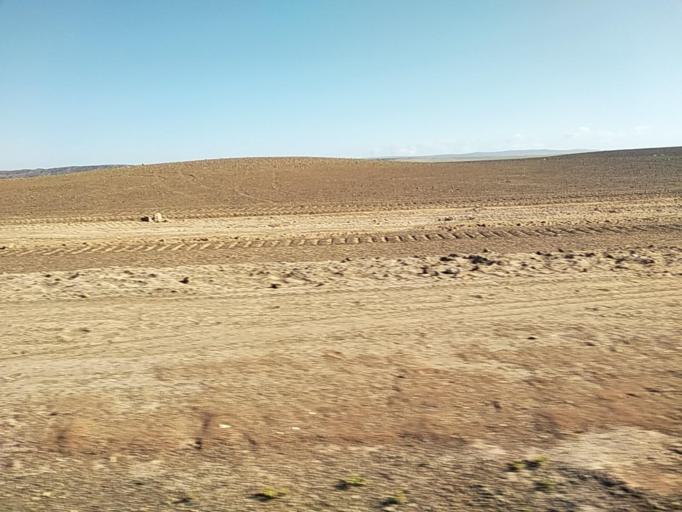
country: CL
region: Atacama
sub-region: Provincia de Copiapo
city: Copiapo
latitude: -27.3240
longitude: -70.8080
